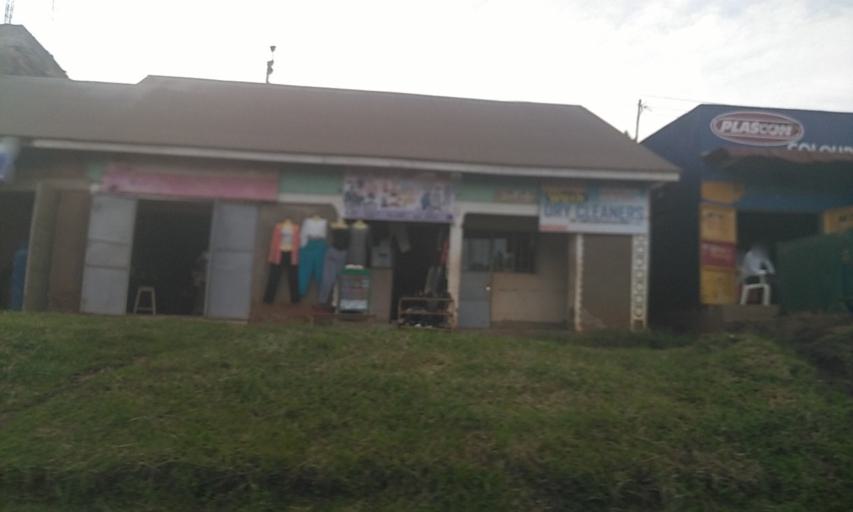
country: UG
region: Central Region
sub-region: Wakiso District
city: Kajansi
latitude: 0.2342
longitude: 32.5530
